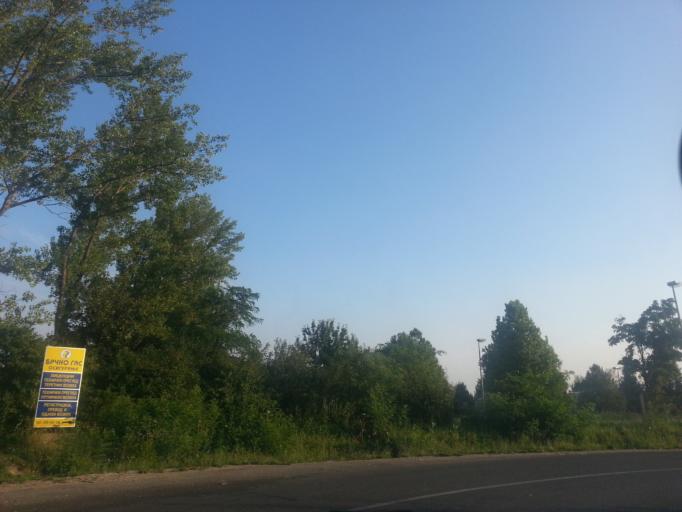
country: BA
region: Brcko
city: Brcko
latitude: 44.8526
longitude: 18.8205
